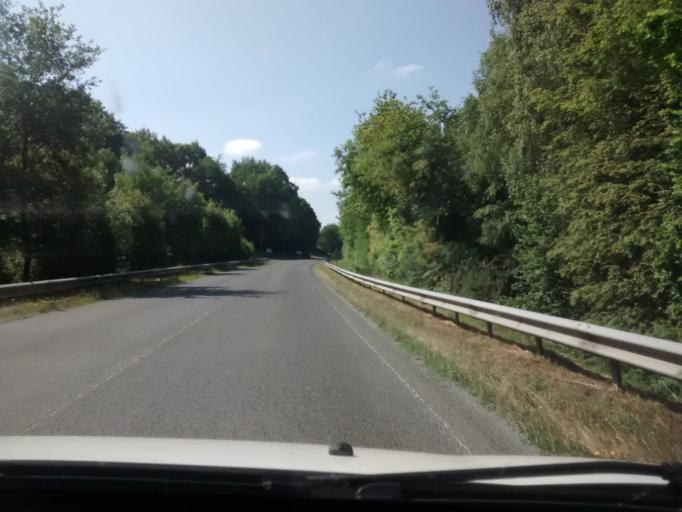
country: FR
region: Pays de la Loire
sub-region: Departement de la Sarthe
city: Vibraye
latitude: 47.9991
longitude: 0.7623
